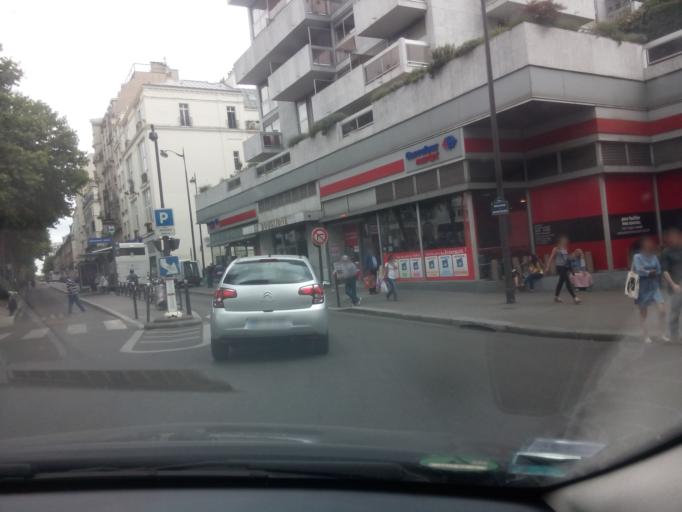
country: FR
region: Ile-de-France
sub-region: Paris
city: Saint-Ouen
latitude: 48.8818
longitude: 2.3393
